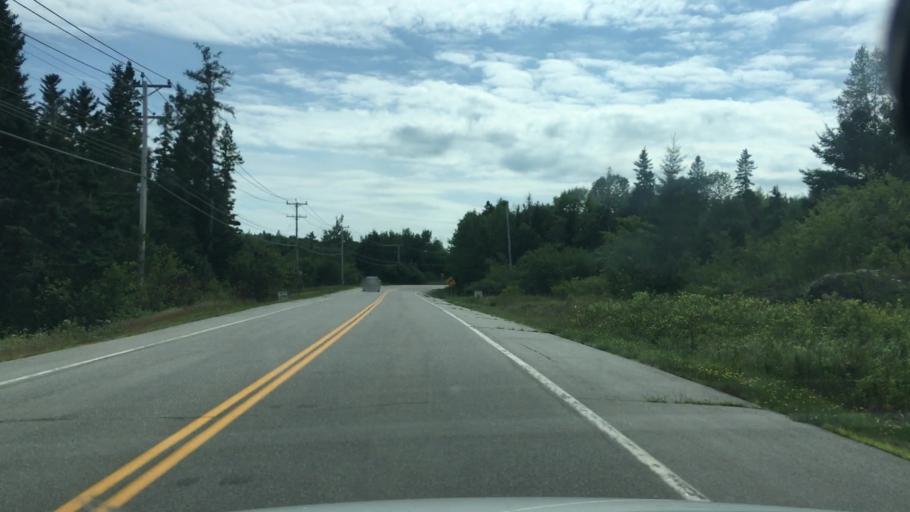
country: US
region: Maine
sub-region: Washington County
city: Eastport
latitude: 44.9532
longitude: -67.1051
